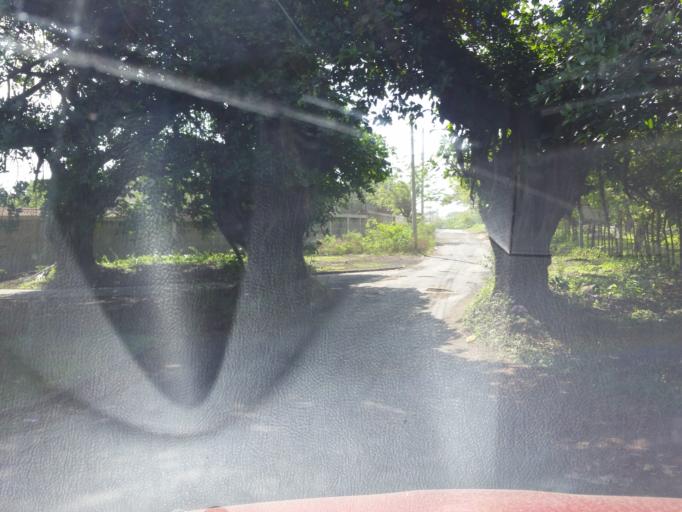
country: NI
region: Managua
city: Managua
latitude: 12.0780
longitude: -86.2504
